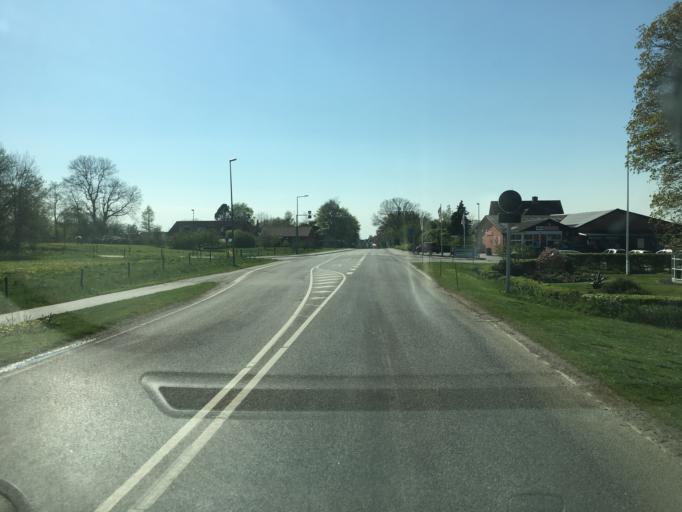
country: DK
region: South Denmark
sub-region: Haderslev Kommune
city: Vojens
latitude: 55.3212
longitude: 9.3115
